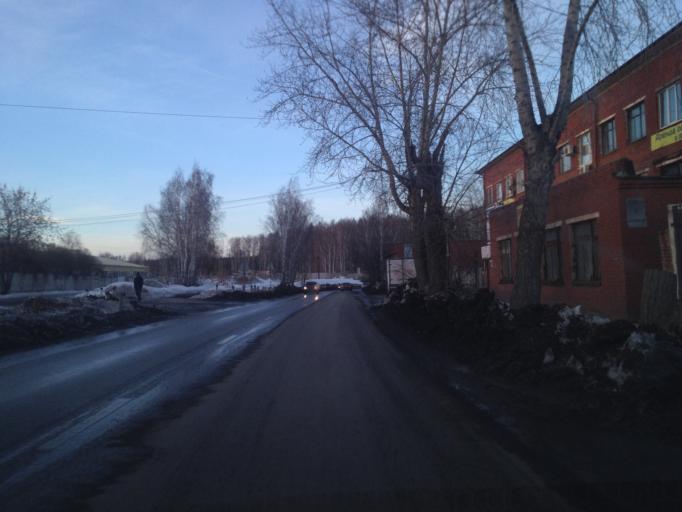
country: RU
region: Sverdlovsk
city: Istok
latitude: 56.7598
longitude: 60.7325
